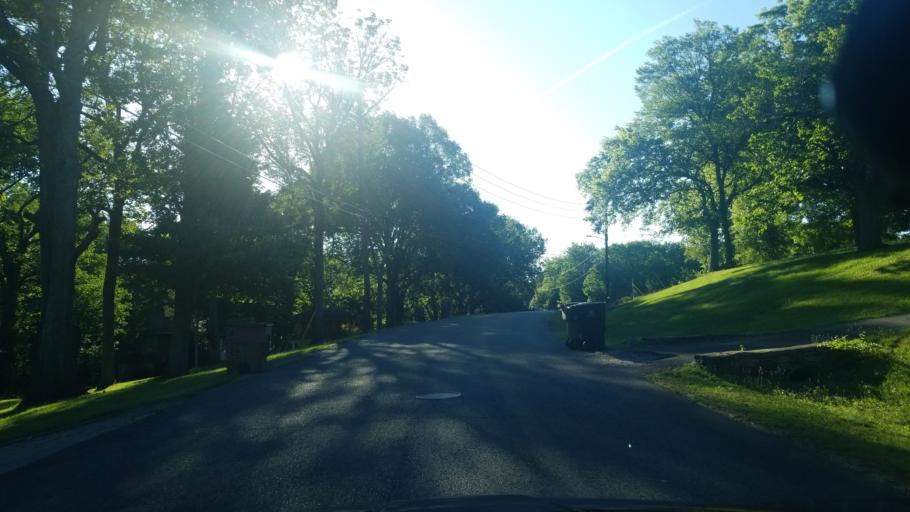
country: US
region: Tennessee
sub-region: Davidson County
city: Nashville
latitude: 36.2399
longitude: -86.7649
